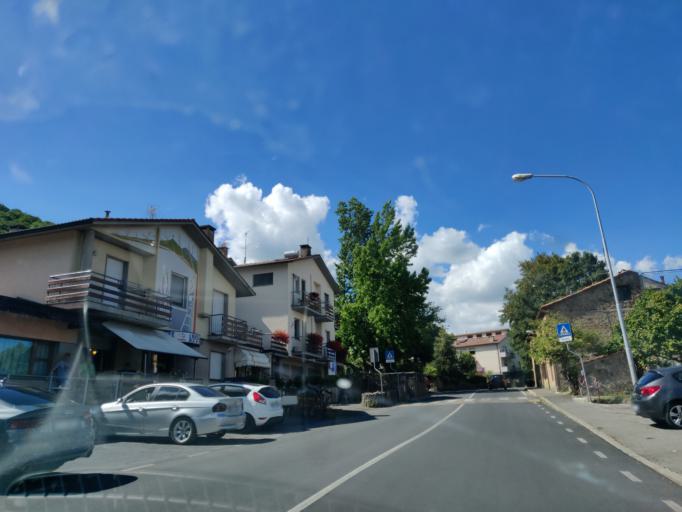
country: IT
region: Tuscany
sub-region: Provincia di Siena
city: Abbadia San Salvatore
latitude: 42.8871
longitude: 11.6675
